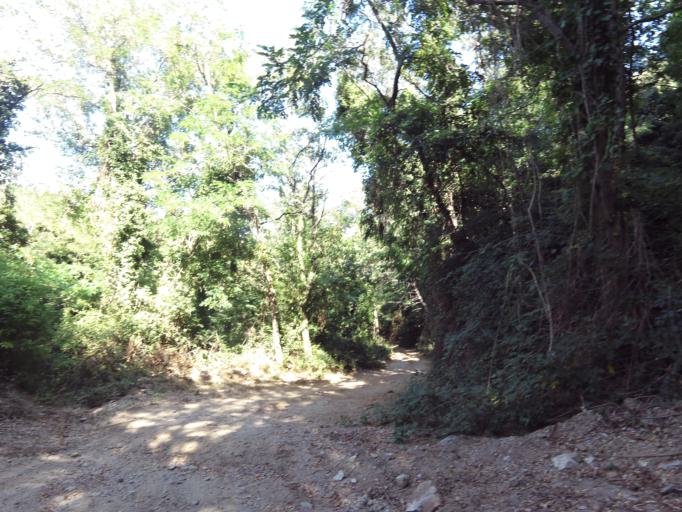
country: IT
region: Calabria
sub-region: Provincia di Reggio Calabria
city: Pazzano
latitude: 38.4699
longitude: 16.4138
